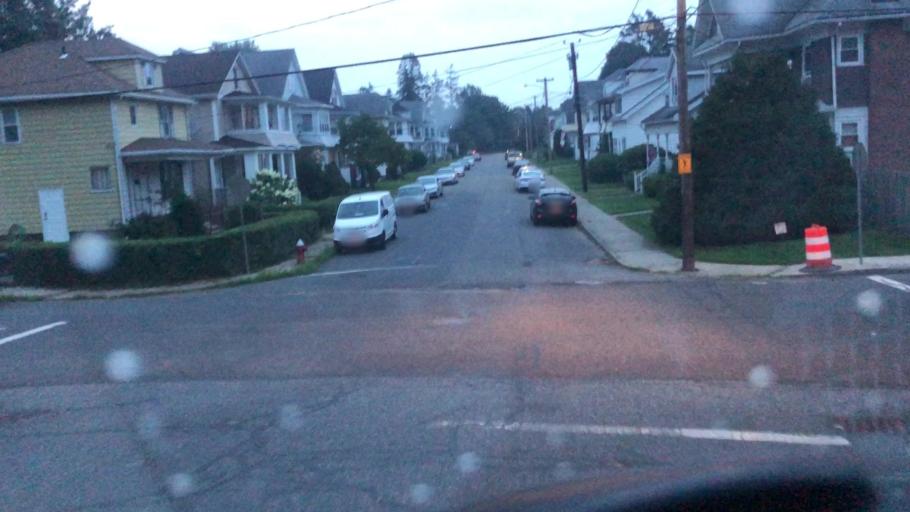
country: US
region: Massachusetts
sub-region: Hampden County
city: Holyoke
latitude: 42.2069
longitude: -72.6338
